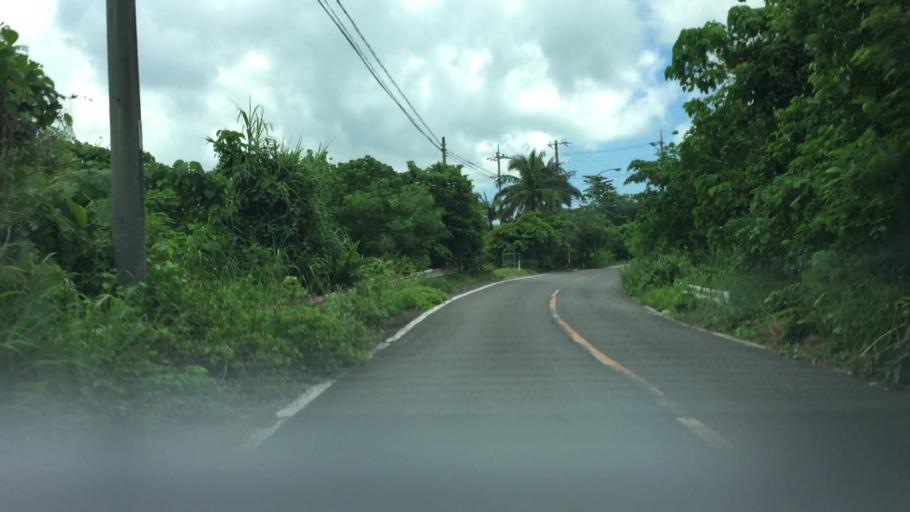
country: JP
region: Okinawa
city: Ishigaki
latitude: 24.3775
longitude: 124.1312
